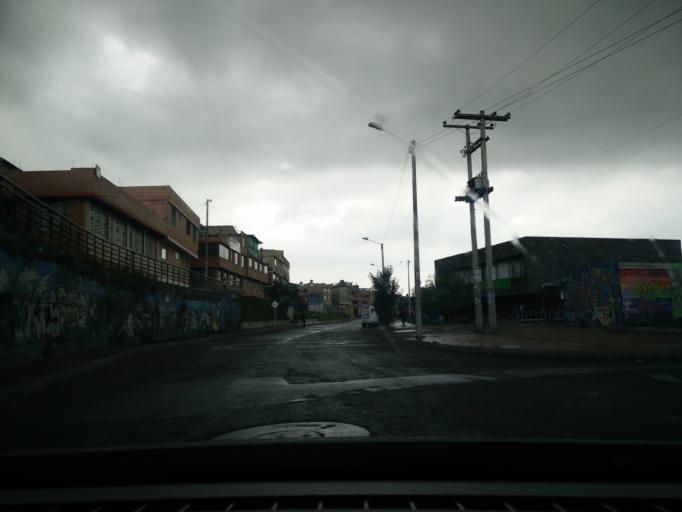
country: CO
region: Cundinamarca
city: Cota
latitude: 4.7494
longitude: -74.1146
